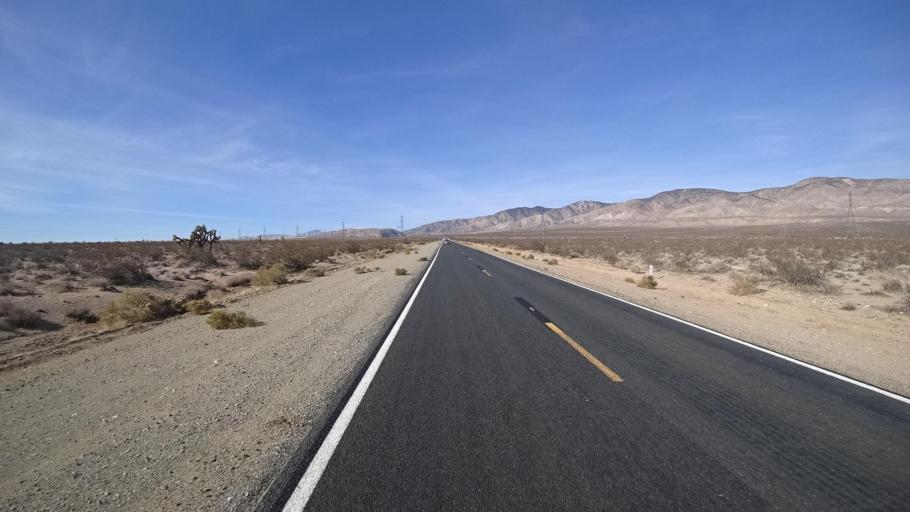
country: US
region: California
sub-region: Kern County
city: Mojave
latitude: 35.1258
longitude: -118.1541
